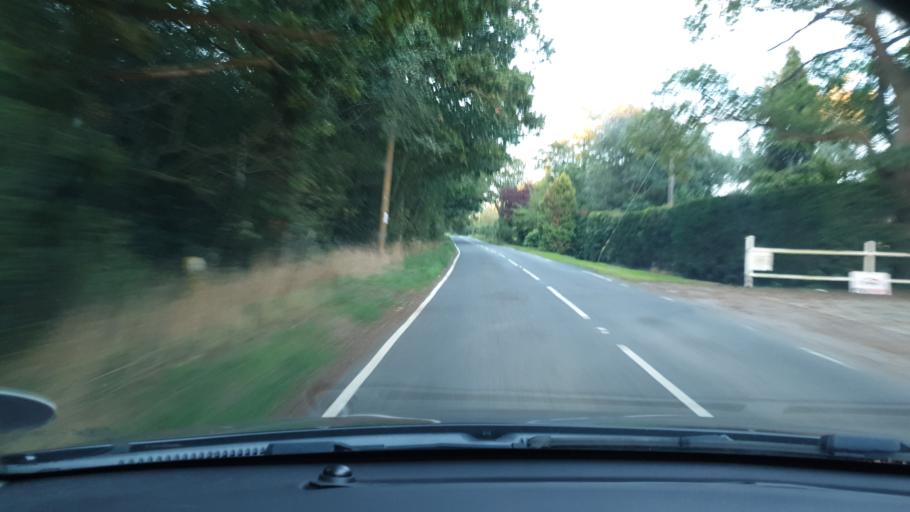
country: GB
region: England
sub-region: Essex
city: Alresford
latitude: 51.9054
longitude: 0.9879
